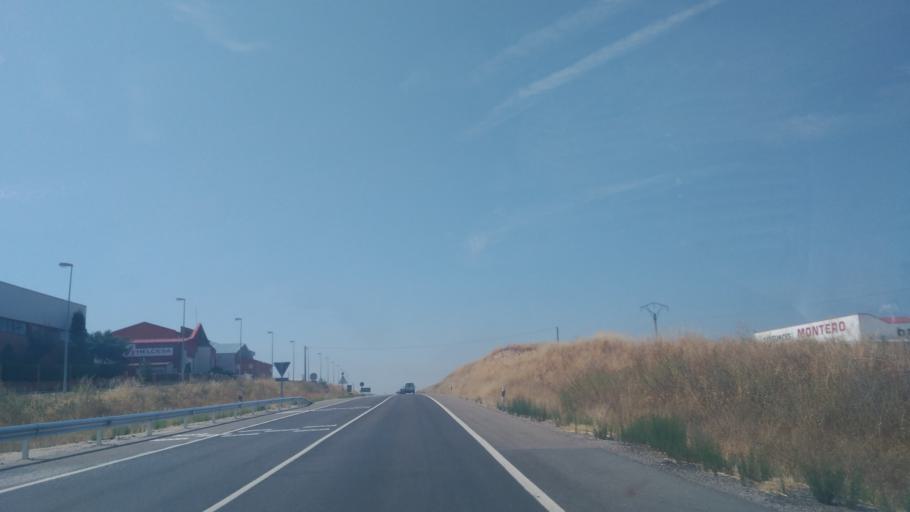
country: ES
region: Castille and Leon
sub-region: Provincia de Salamanca
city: San Cristobal de la Cuesta
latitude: 41.0097
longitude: -5.6120
